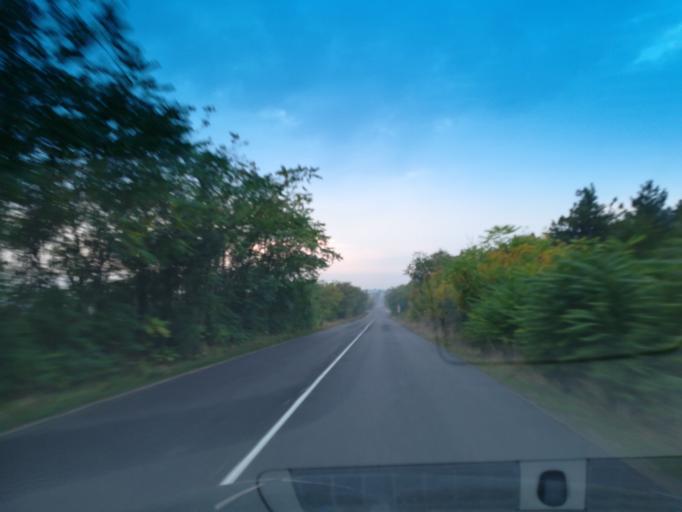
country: BG
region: Stara Zagora
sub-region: Obshtina Chirpan
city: Chirpan
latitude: 42.1884
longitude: 25.2779
